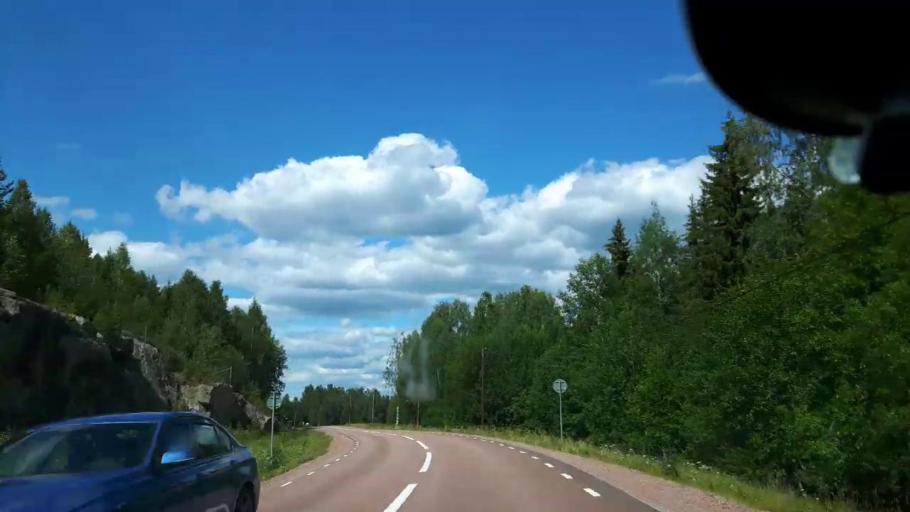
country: SE
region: Jaemtland
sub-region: Ragunda Kommun
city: Hammarstrand
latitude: 63.0389
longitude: 16.5186
